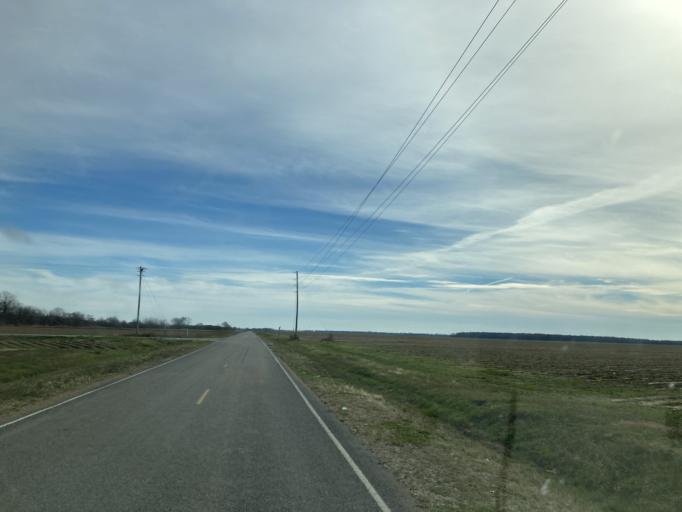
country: US
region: Mississippi
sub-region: Humphreys County
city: Belzoni
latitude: 33.0632
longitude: -90.6165
